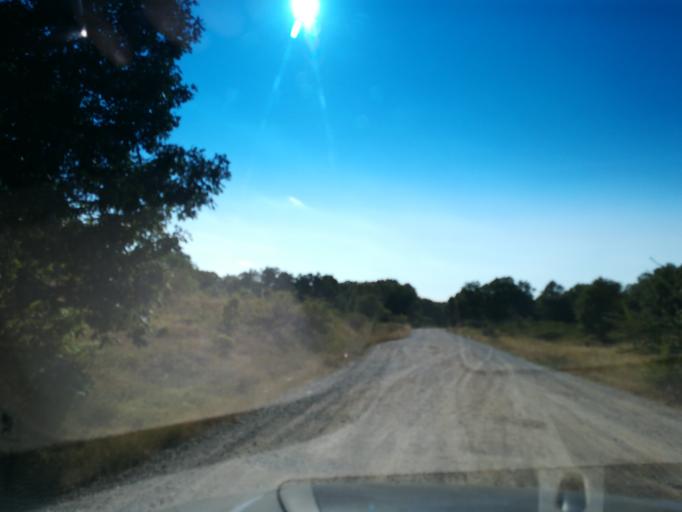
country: BG
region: Khaskovo
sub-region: Obshtina Mineralni Bani
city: Mineralni Bani
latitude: 41.9716
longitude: 25.3351
